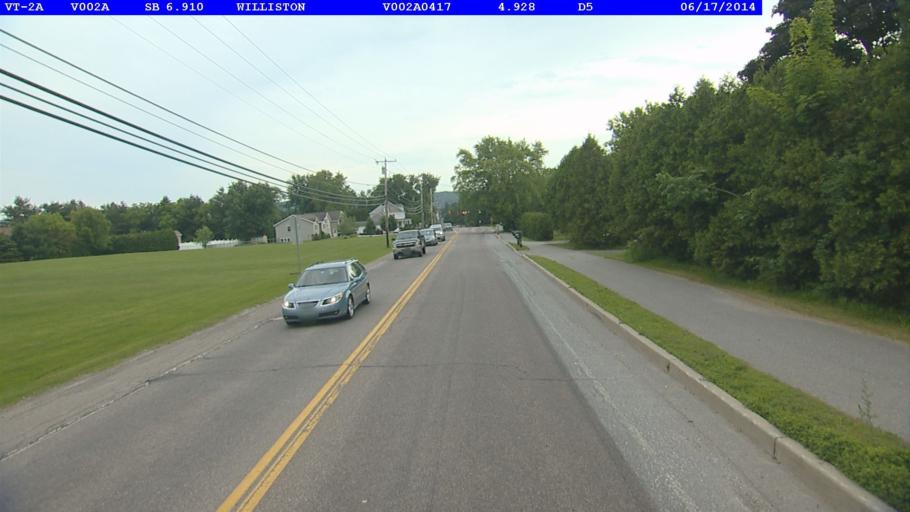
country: US
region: Vermont
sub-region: Chittenden County
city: Essex Junction
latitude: 44.4670
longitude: -73.1130
